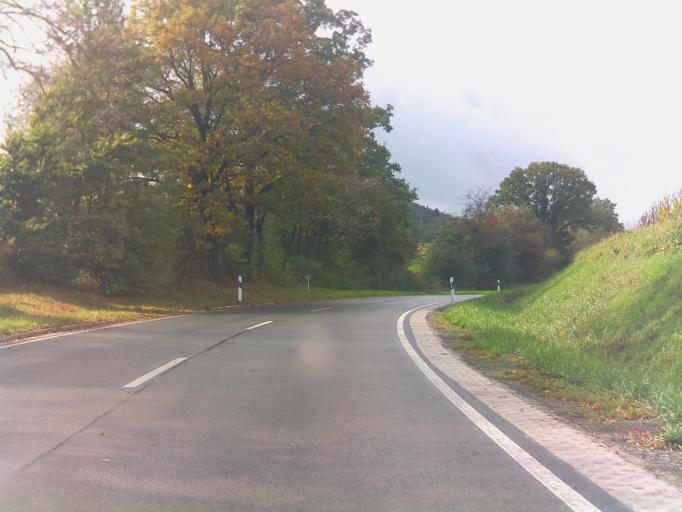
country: DE
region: Bavaria
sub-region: Upper Franconia
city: Burgwindheim
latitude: 49.8855
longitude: 10.5237
